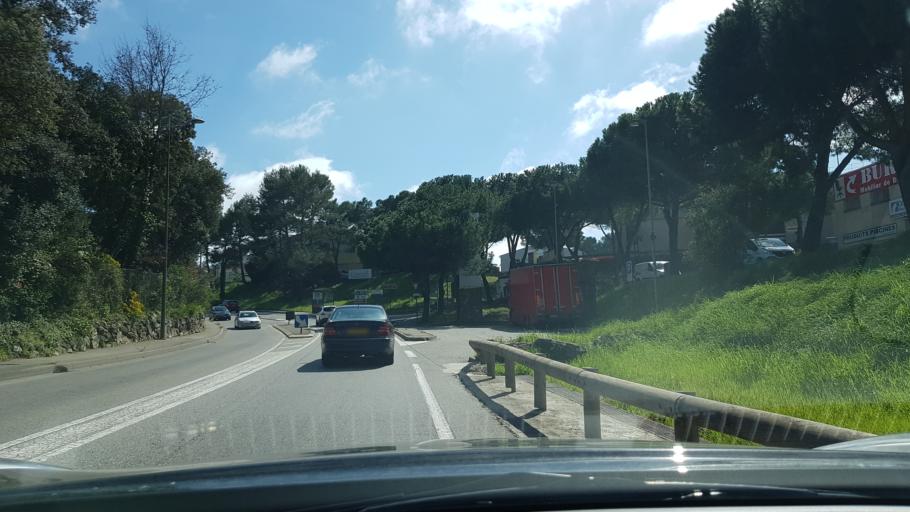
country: FR
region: Provence-Alpes-Cote d'Azur
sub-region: Departement des Alpes-Maritimes
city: Vallauris
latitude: 43.5964
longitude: 7.0574
